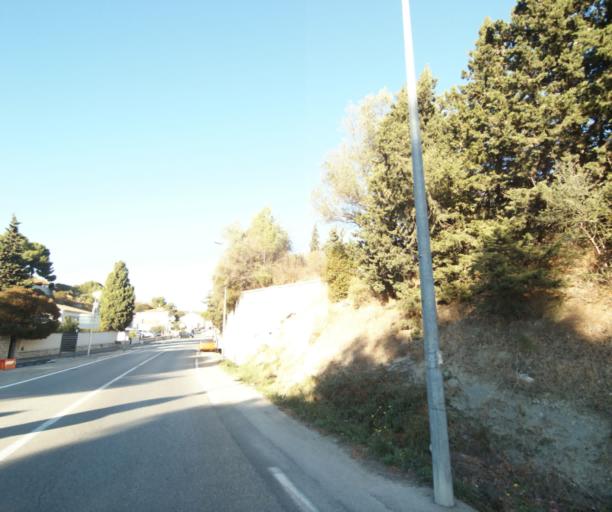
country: FR
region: Provence-Alpes-Cote d'Azur
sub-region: Departement des Bouches-du-Rhone
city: Cassis
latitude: 43.2218
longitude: 5.5438
